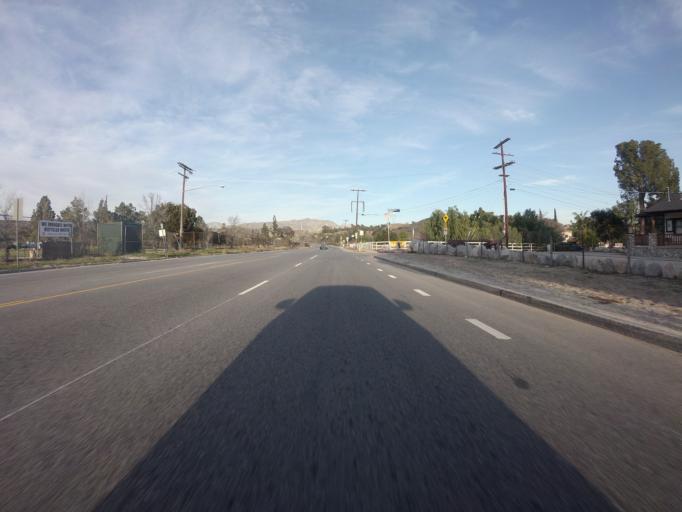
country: US
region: California
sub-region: Los Angeles County
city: San Fernando
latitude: 34.2566
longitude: -118.3759
